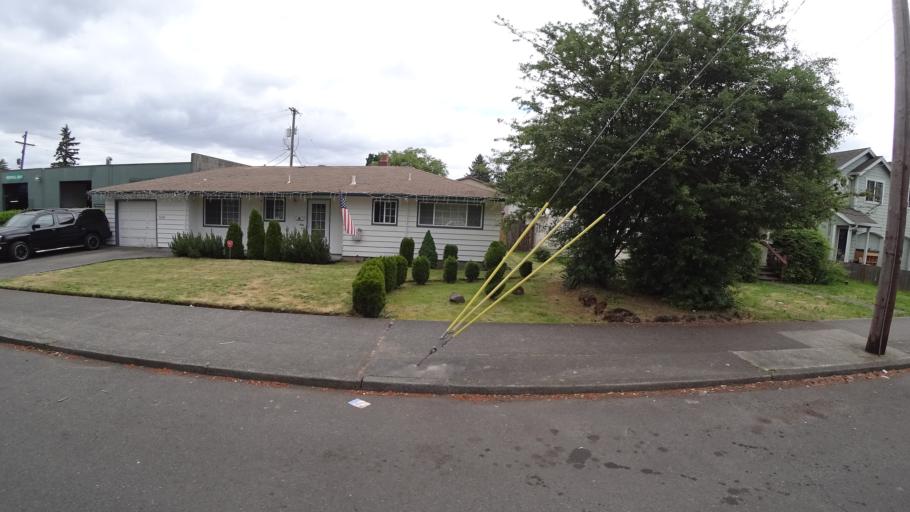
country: US
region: Oregon
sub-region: Multnomah County
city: Lents
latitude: 45.4817
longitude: -122.5780
